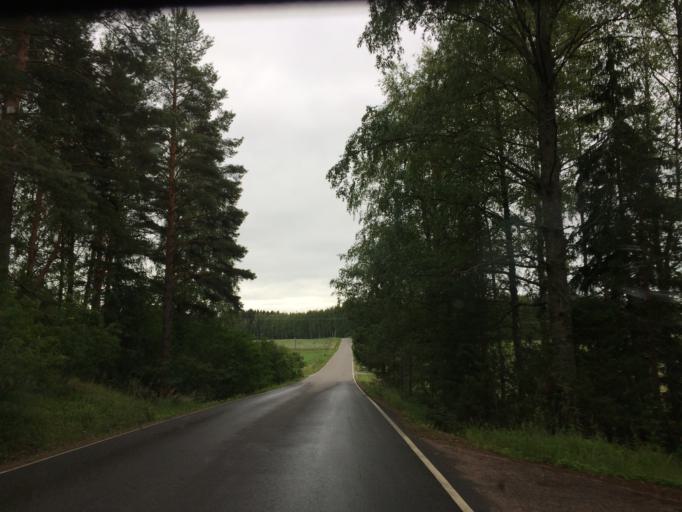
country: FI
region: Haeme
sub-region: Haemeenlinna
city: Janakkala
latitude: 60.8500
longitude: 24.5266
